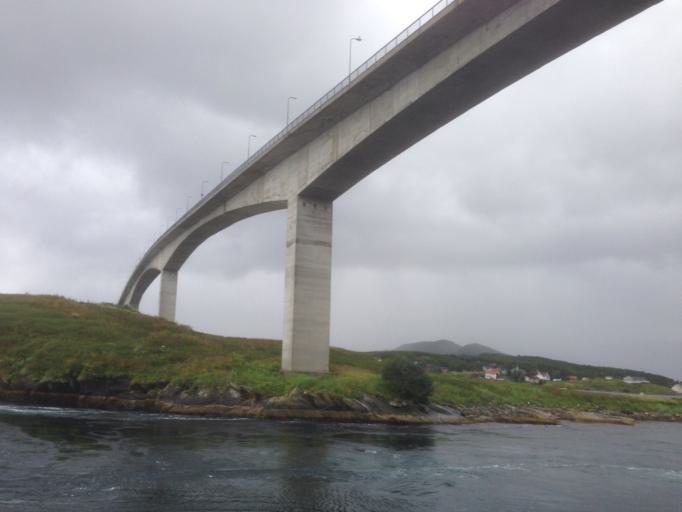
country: NO
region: Nordland
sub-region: Bodo
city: Loding
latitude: 67.2303
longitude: 14.6070
